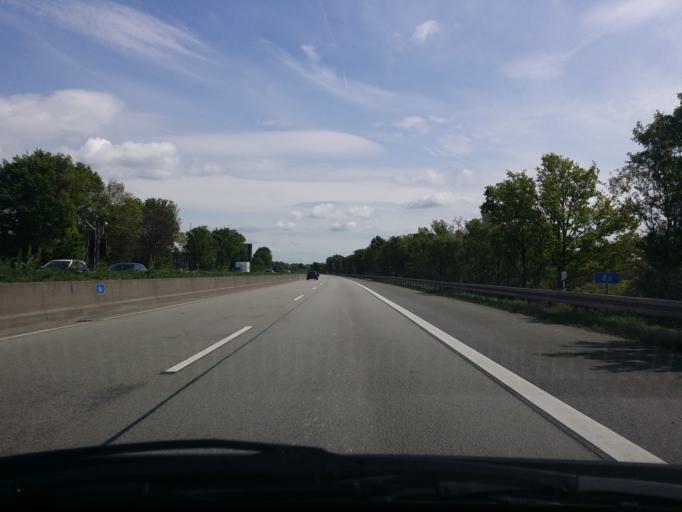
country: DE
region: Rheinland-Pfalz
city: Mainz
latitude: 50.0282
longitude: 8.3027
